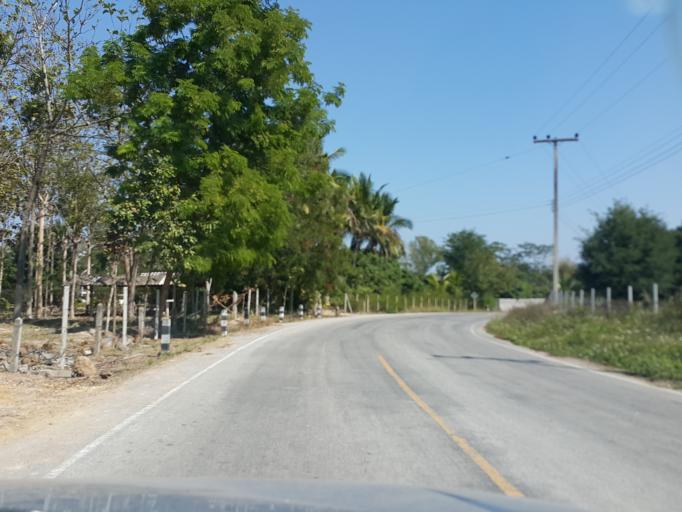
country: TH
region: Chiang Mai
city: Doi Lo
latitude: 18.5361
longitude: 98.7847
